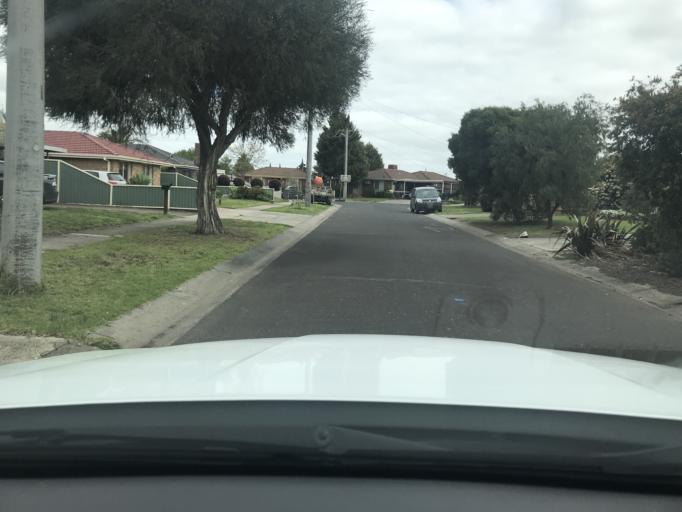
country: AU
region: Victoria
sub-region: Hume
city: Craigieburn
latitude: -37.5940
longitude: 144.9251
